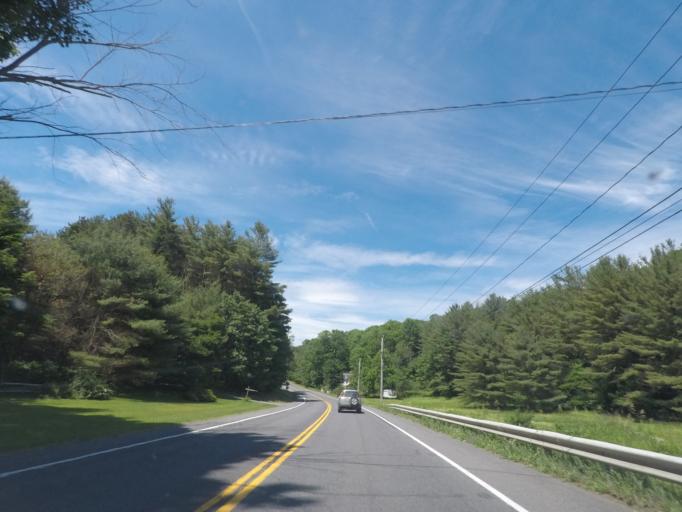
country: US
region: Massachusetts
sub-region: Berkshire County
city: Richmond
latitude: 42.3977
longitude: -73.4089
